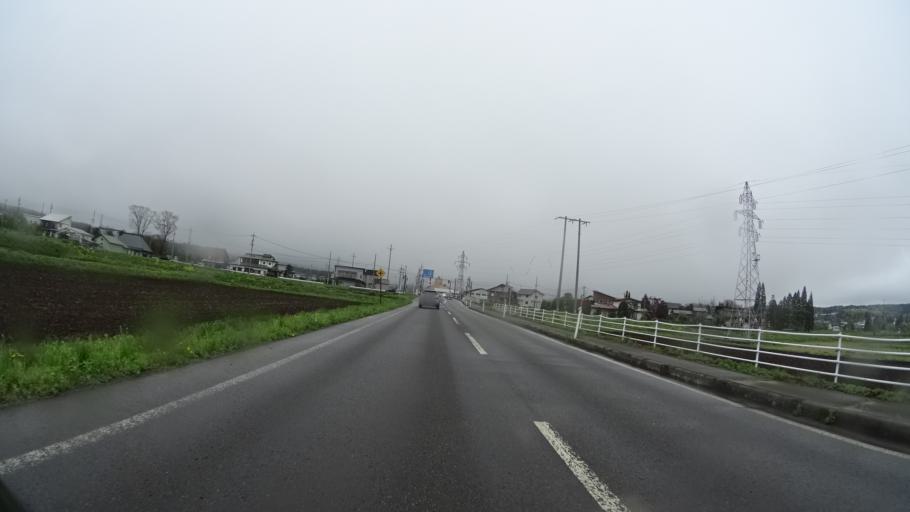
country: JP
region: Nagano
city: Nagano-shi
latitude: 36.8004
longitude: 138.1944
